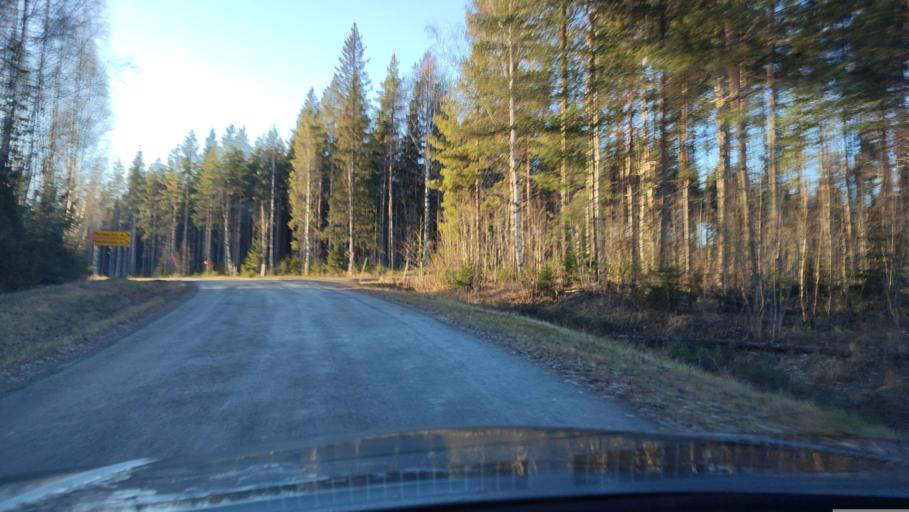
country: SE
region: Vaesterbotten
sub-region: Skelleftea Kommun
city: Viken
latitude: 64.7162
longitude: 20.9138
